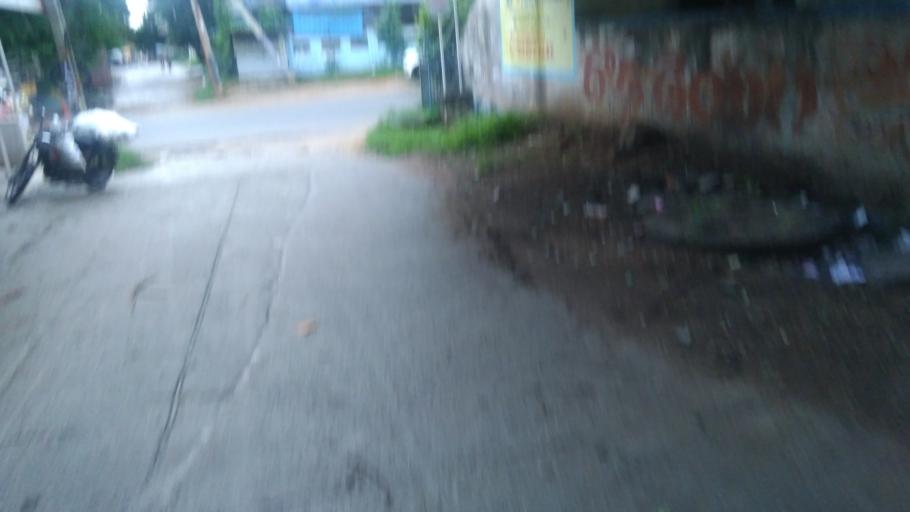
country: IN
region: Telangana
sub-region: Rangareddi
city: Secunderabad
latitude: 17.4797
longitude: 78.5372
